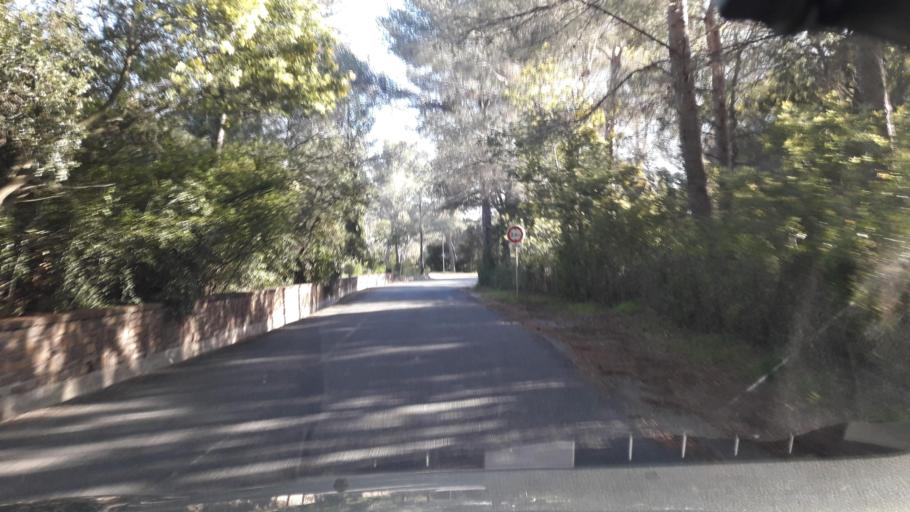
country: FR
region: Provence-Alpes-Cote d'Azur
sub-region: Departement du Var
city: Saint-Raphael
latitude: 43.4221
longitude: 6.8232
